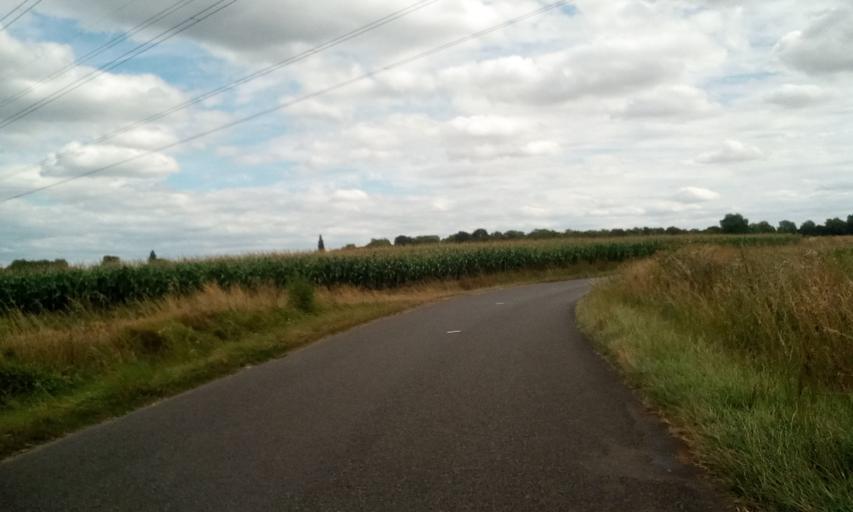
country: FR
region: Lower Normandy
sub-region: Departement du Calvados
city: Bellengreville
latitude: 49.1334
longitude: -0.2033
